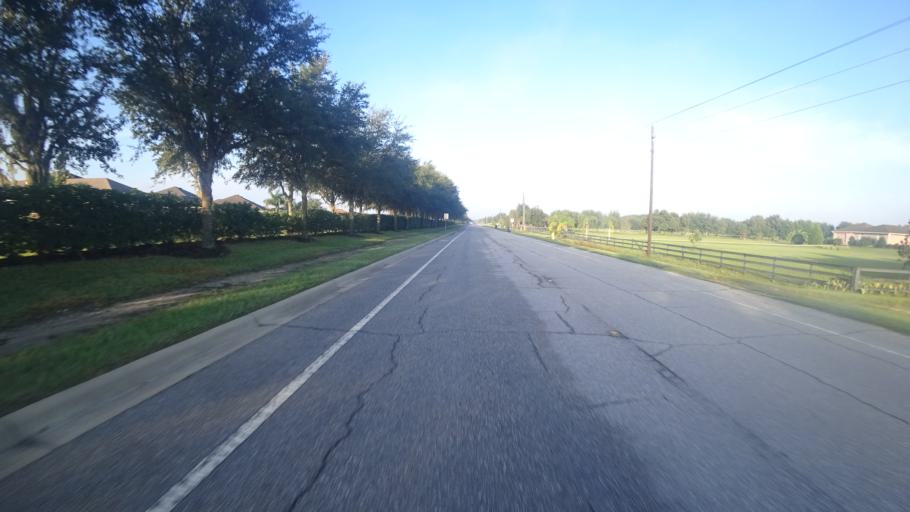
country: US
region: Florida
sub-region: Manatee County
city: Ellenton
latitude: 27.5354
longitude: -82.4079
